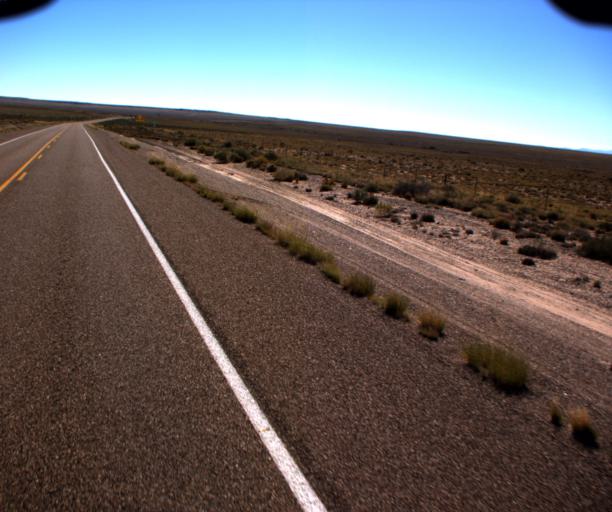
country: US
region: Arizona
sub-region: Navajo County
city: Holbrook
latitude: 34.8498
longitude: -109.9656
